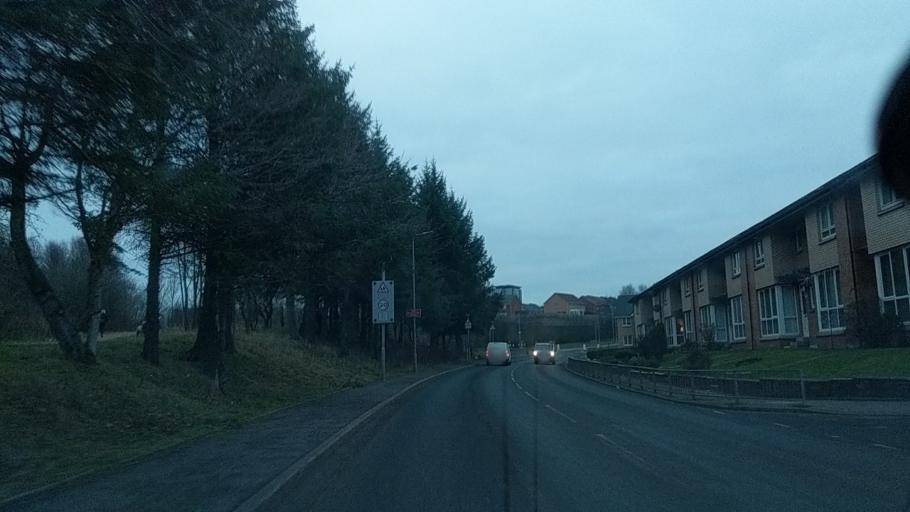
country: GB
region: Scotland
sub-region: South Lanarkshire
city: Rutherglen
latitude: 55.8134
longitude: -4.1855
